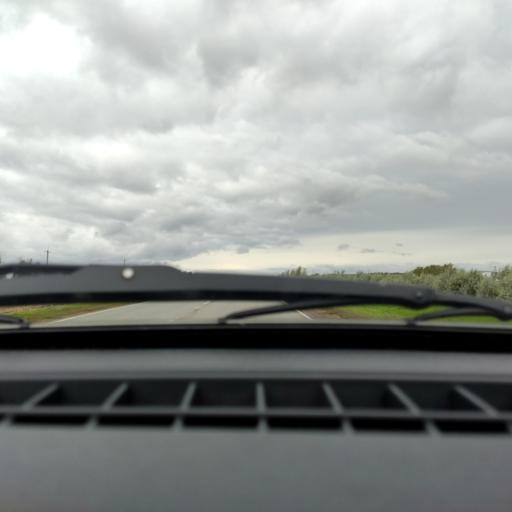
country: RU
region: Bashkortostan
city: Rayevskiy
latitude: 54.0825
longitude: 54.9118
